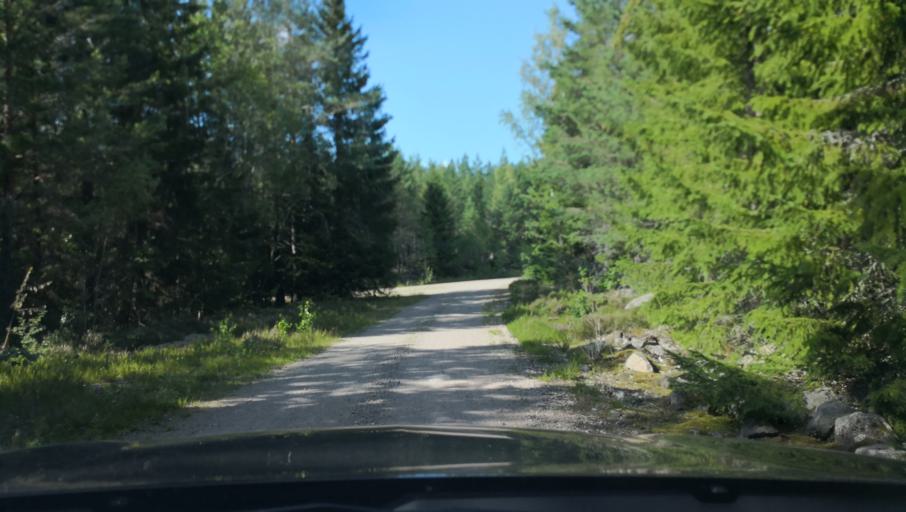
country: SE
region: Vaestmanland
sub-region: Vasteras
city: Skultuna
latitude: 59.7112
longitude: 16.3703
